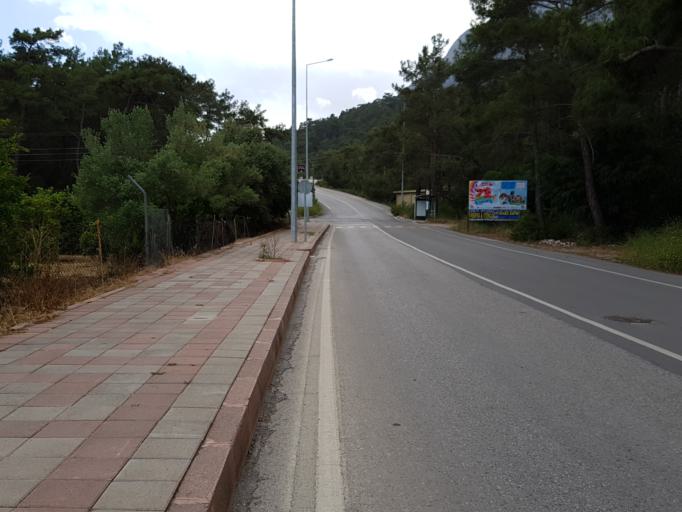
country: TR
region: Antalya
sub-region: Kemer
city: Goeynuek
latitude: 36.6448
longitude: 30.5484
